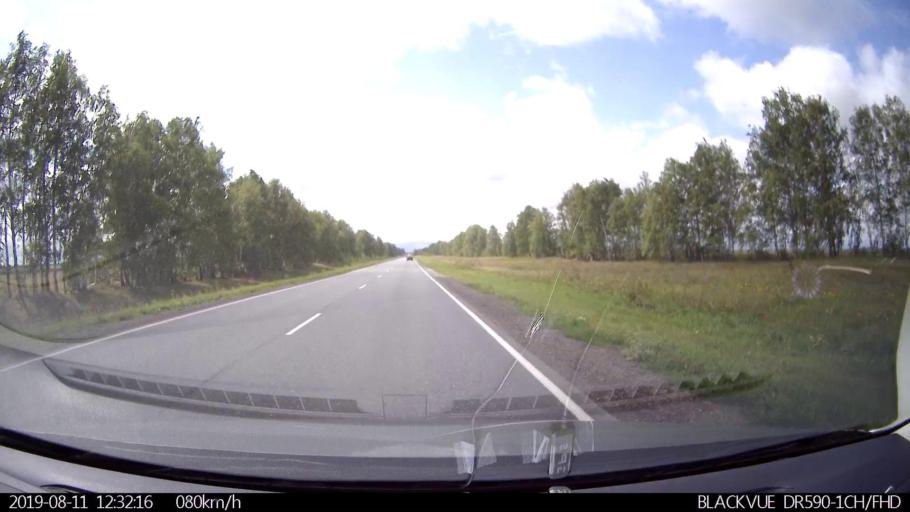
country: RU
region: Ulyanovsk
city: Ignatovka
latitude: 53.8154
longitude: 47.8718
